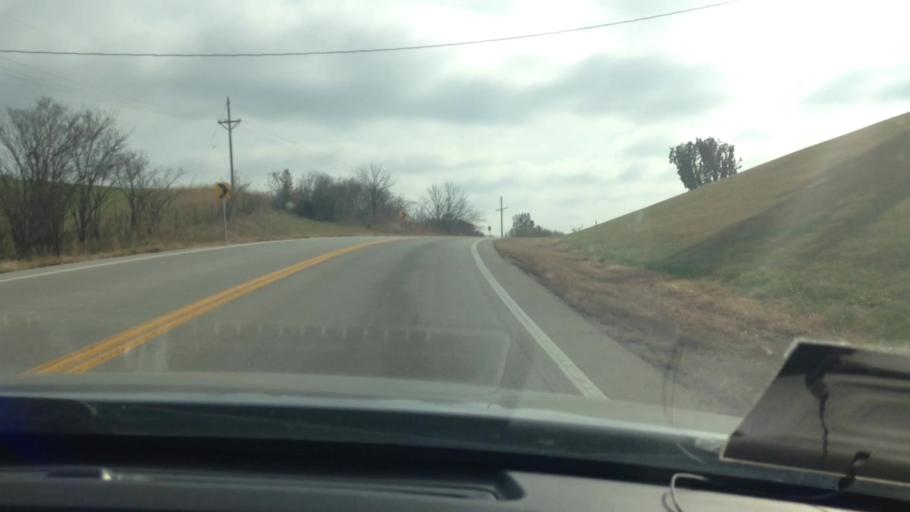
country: US
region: Missouri
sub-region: Platte County
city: Weatherby Lake
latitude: 39.2321
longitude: -94.7825
